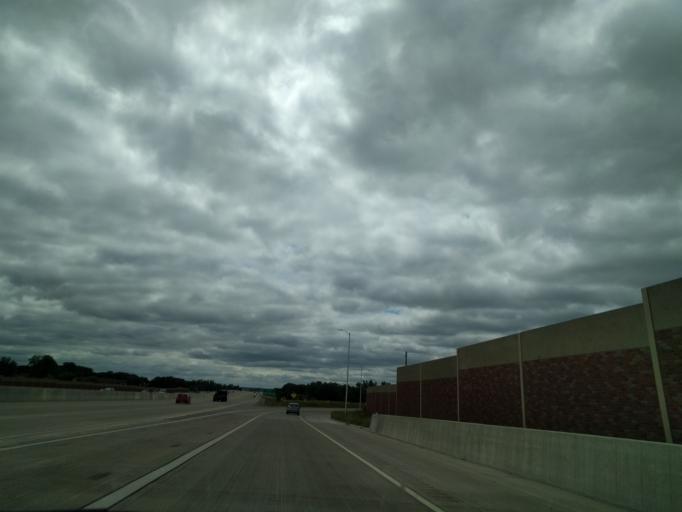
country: US
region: Wisconsin
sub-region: Brown County
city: Ashwaubenon
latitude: 44.4920
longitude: -88.0815
